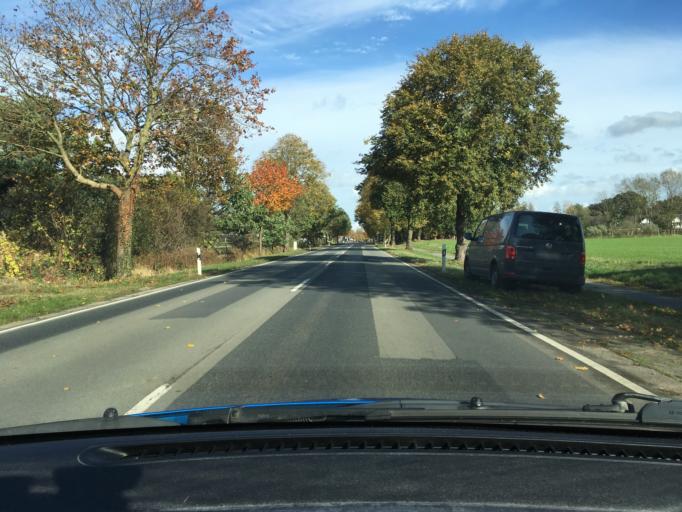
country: DE
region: Lower Saxony
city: Wistedt
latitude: 53.2756
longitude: 9.6900
